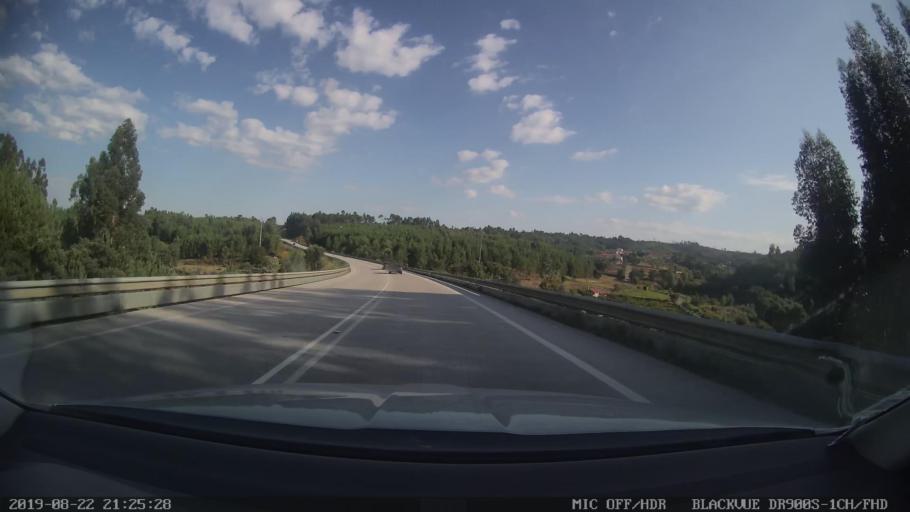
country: PT
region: Castelo Branco
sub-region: Serta
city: Serta
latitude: 39.8546
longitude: -8.1242
